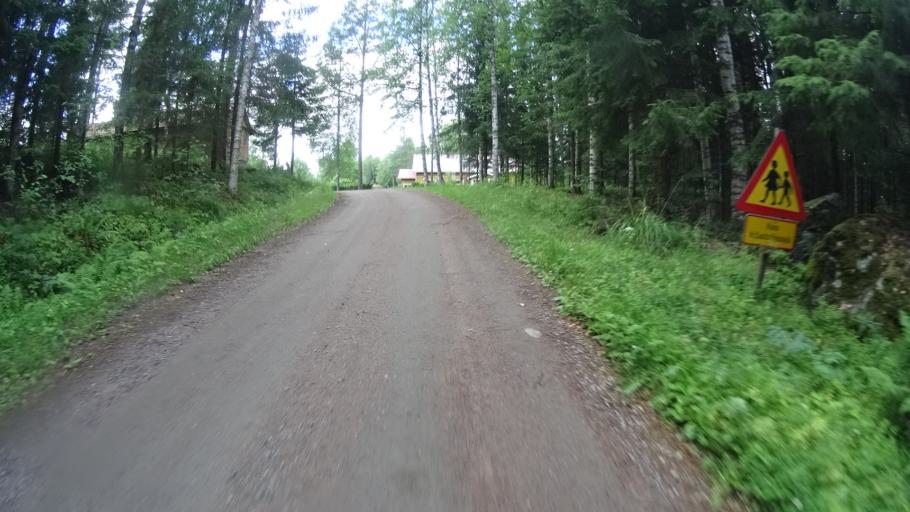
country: FI
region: Uusimaa
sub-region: Helsinki
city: Karkkila
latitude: 60.6019
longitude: 24.2078
